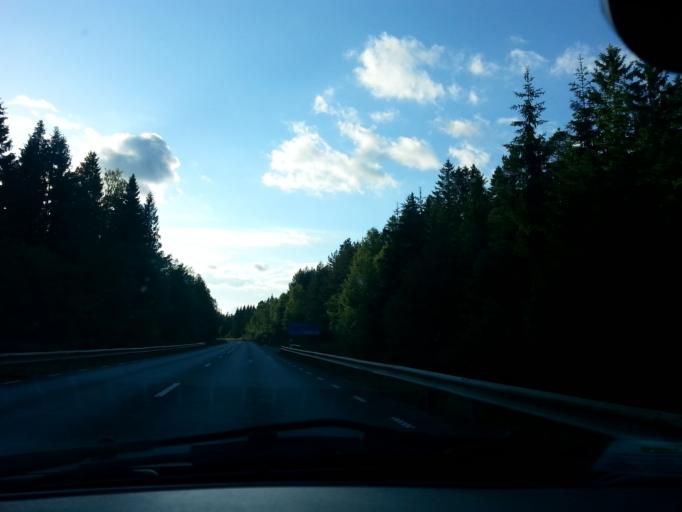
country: SE
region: Joenkoeping
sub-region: Gislaveds Kommun
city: Gislaved
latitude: 57.3339
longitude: 13.5191
